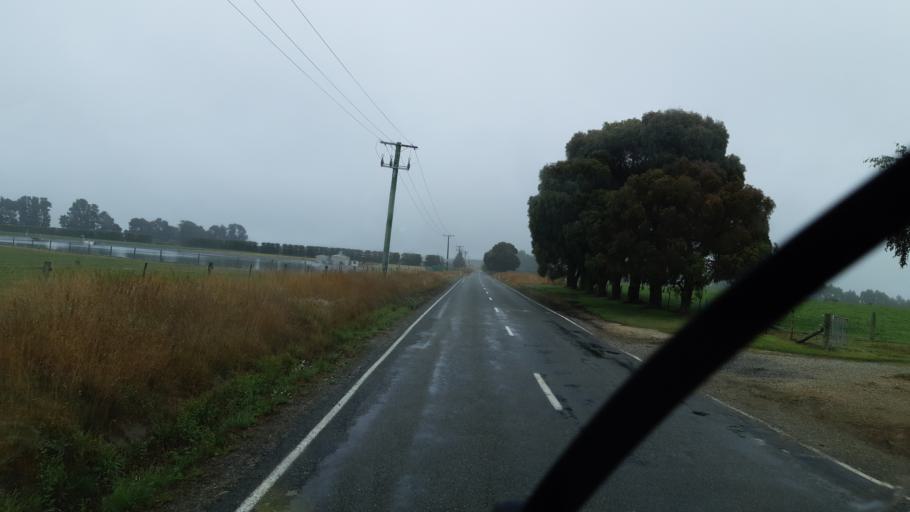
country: NZ
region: Otago
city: Oamaru
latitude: -44.9296
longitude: 170.7899
